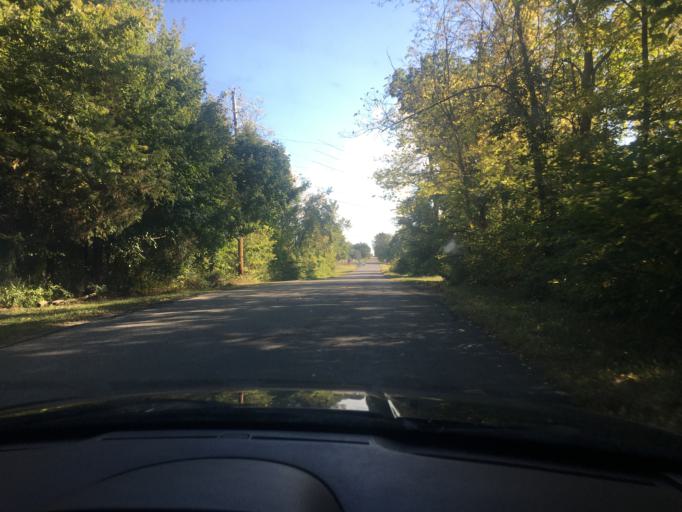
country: US
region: Ohio
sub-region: Logan County
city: Russells Point
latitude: 40.4601
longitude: -83.8570
